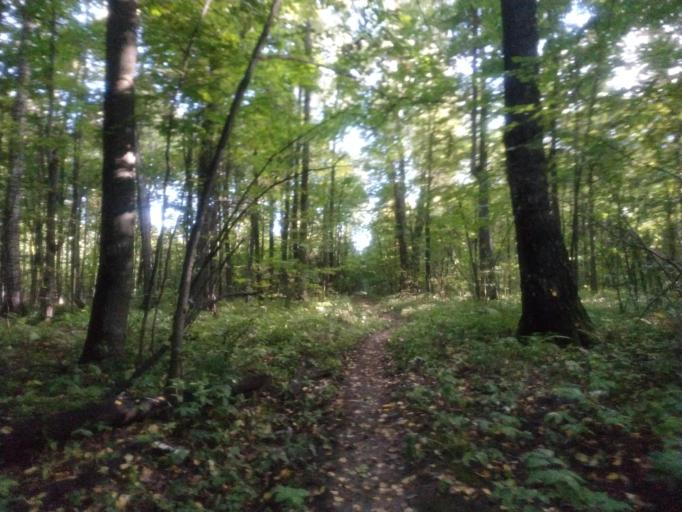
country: RU
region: Chuvashia
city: Novyye Lapsary
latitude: 56.1359
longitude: 47.1102
